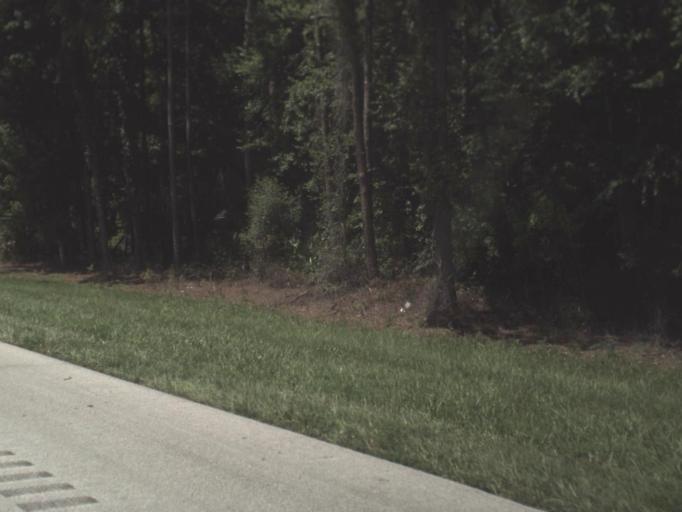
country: US
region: Florida
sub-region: Saint Johns County
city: Saint Augustine
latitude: 29.8704
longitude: -81.3979
